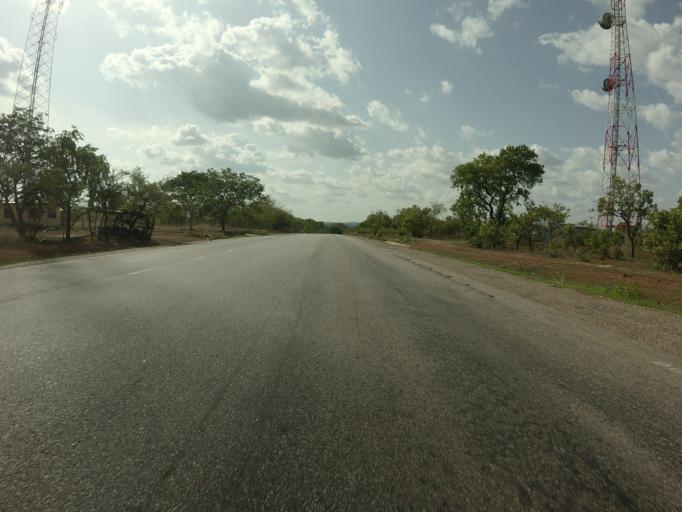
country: GH
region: Upper East
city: Bolgatanga
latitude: 10.5512
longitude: -0.8292
